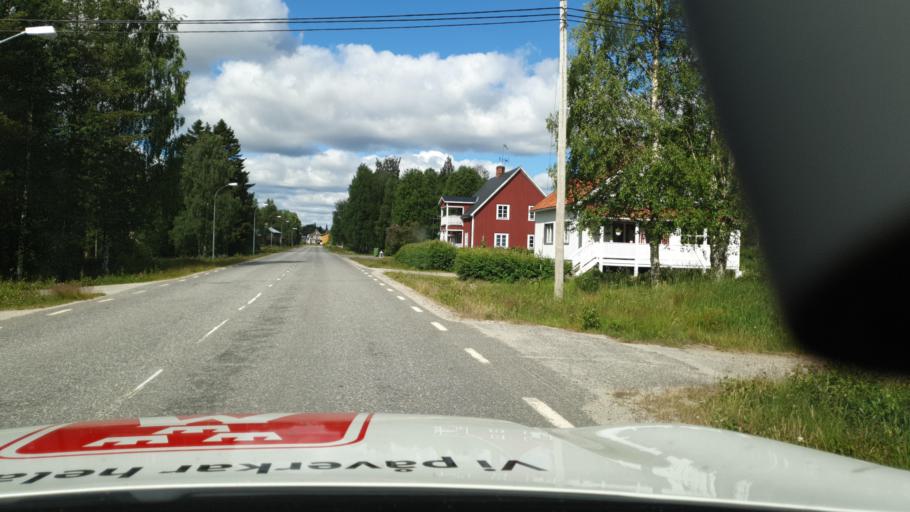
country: SE
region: Vaesterbotten
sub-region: Mala Kommun
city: Mala
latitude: 64.9863
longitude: 18.5273
